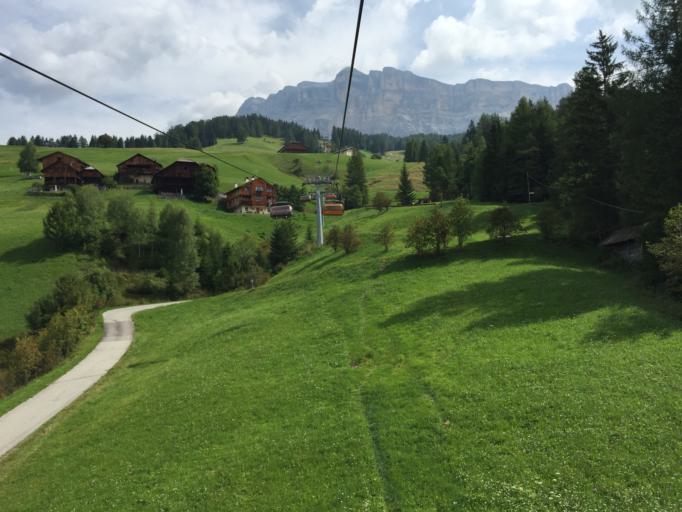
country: IT
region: Trentino-Alto Adige
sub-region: Bolzano
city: Badia
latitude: 46.6100
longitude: 11.9027
